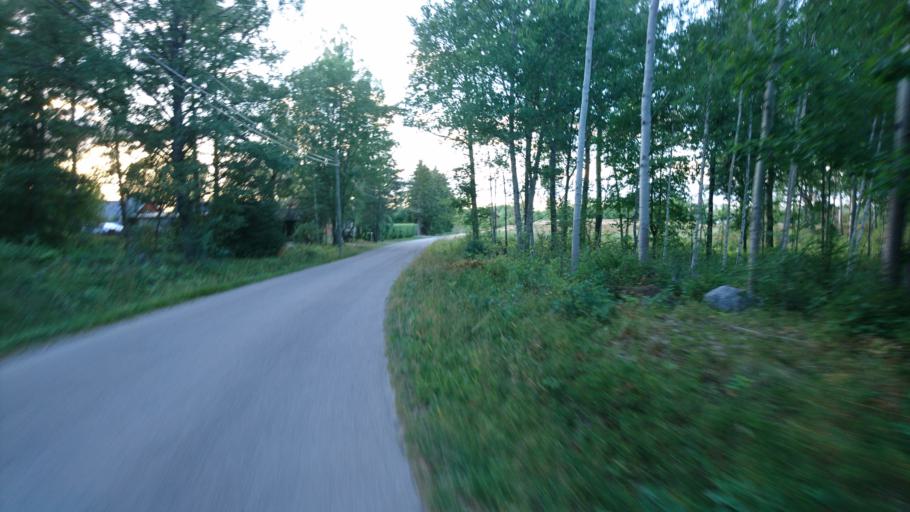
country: SE
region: Soedermanland
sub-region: Strangnas Kommun
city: Stallarholmen
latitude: 59.3988
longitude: 17.3022
